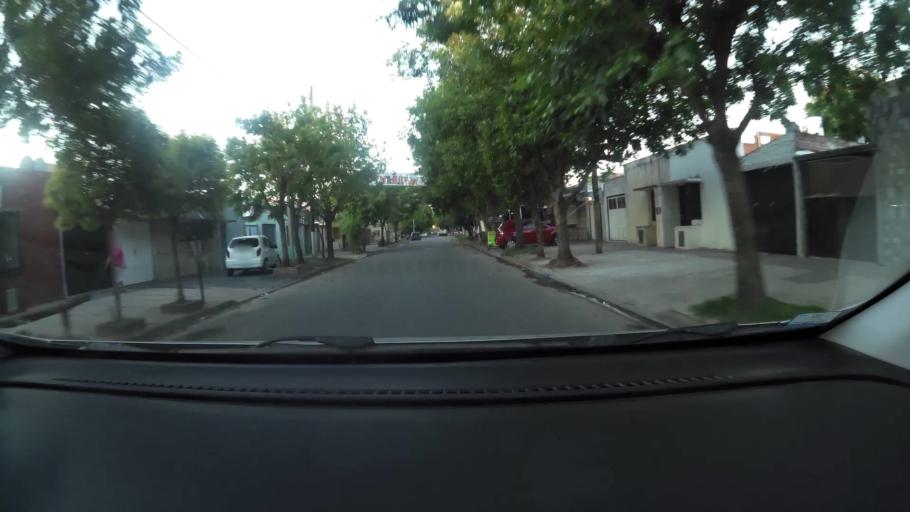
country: AR
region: Santa Fe
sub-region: Departamento de Rosario
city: Rosario
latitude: -32.9698
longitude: -60.6883
